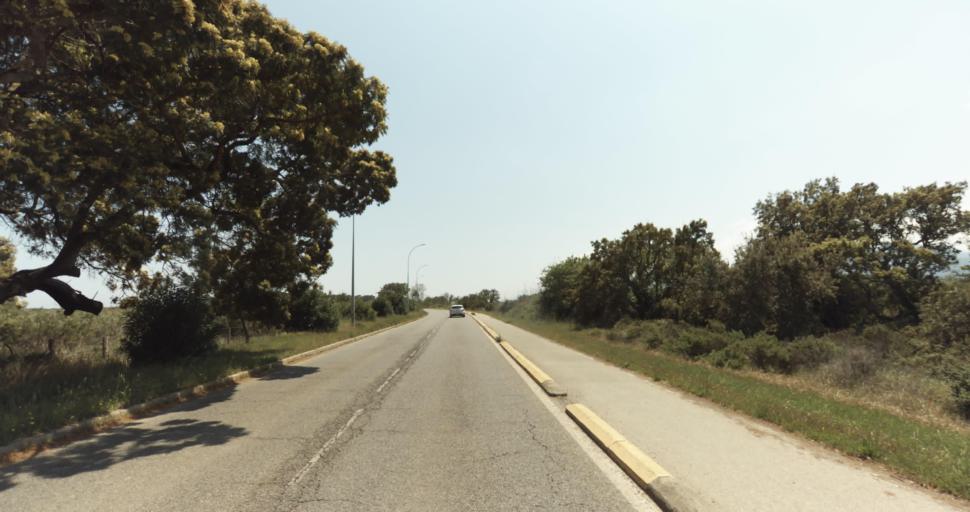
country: FR
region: Corsica
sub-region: Departement de la Haute-Corse
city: Biguglia
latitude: 42.6535
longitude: 9.4503
